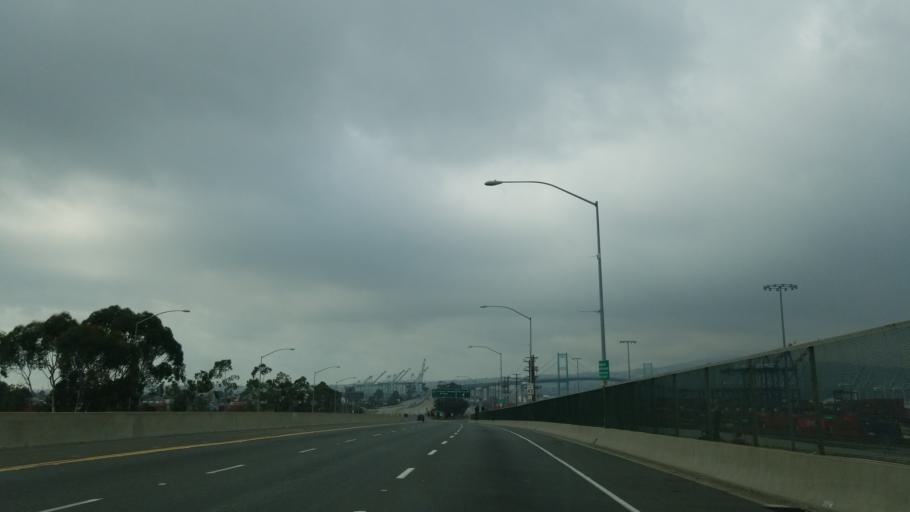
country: US
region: California
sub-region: Los Angeles County
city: San Pedro
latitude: 33.7537
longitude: -118.2528
